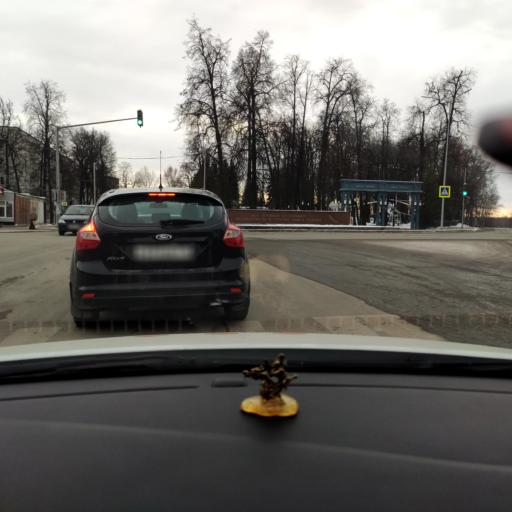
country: RU
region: Tatarstan
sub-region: Zelenodol'skiy Rayon
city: Zelenodolsk
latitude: 55.8468
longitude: 48.5010
